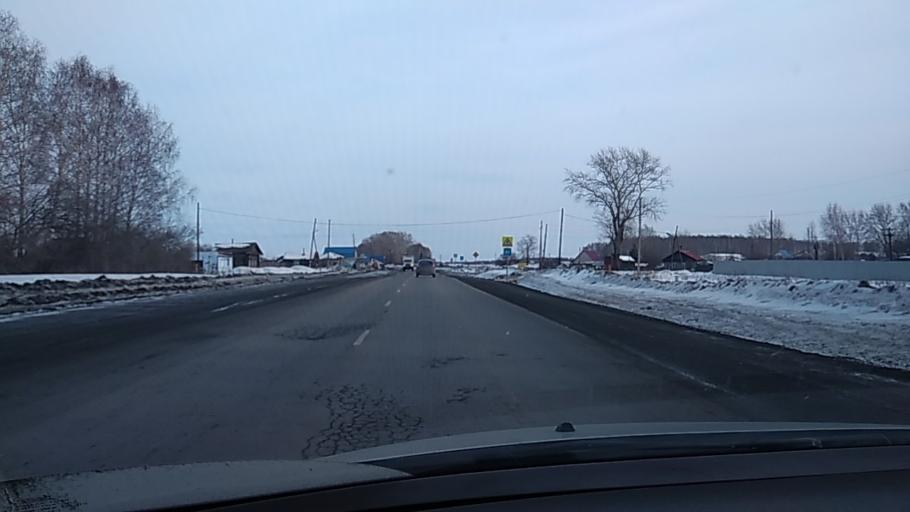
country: RU
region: Sverdlovsk
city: Pokrovskoye
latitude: 56.4703
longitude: 61.6670
